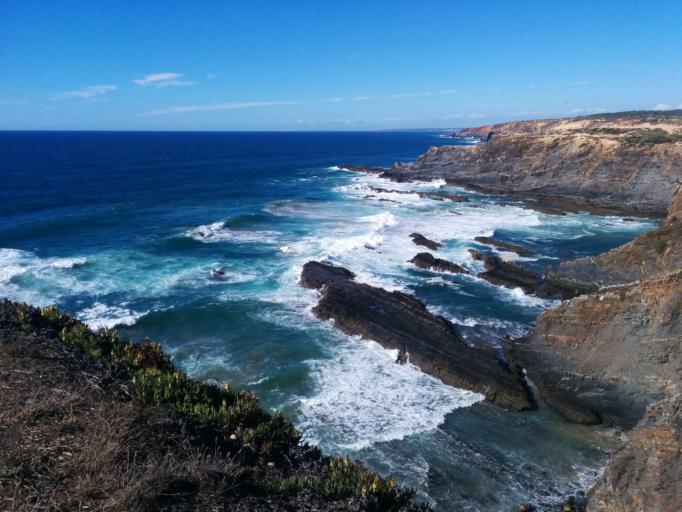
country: PT
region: Beja
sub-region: Odemira
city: Vila Nova de Milfontes
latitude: 37.6009
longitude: -8.8173
